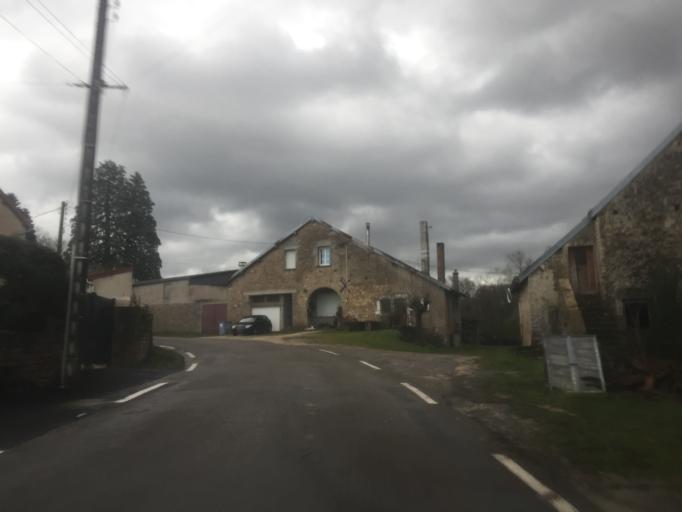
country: FR
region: Franche-Comte
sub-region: Departement de la Haute-Saone
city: Pesmes
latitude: 47.2176
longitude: 5.5228
